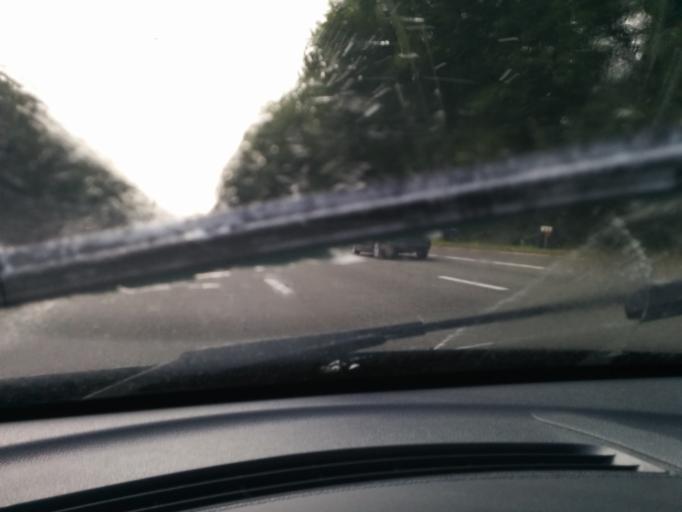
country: BE
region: Flanders
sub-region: Provincie Vlaams-Brabant
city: Ternat
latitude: 50.8829
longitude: 4.1637
